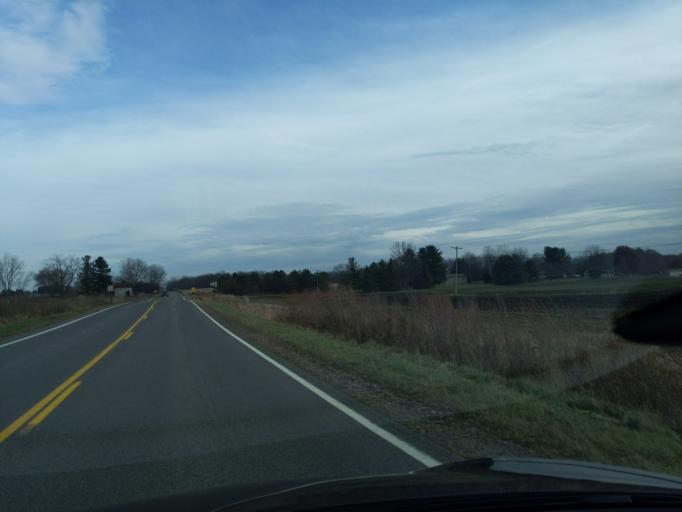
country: US
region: Michigan
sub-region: Ingham County
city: Mason
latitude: 42.6400
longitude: -84.4070
